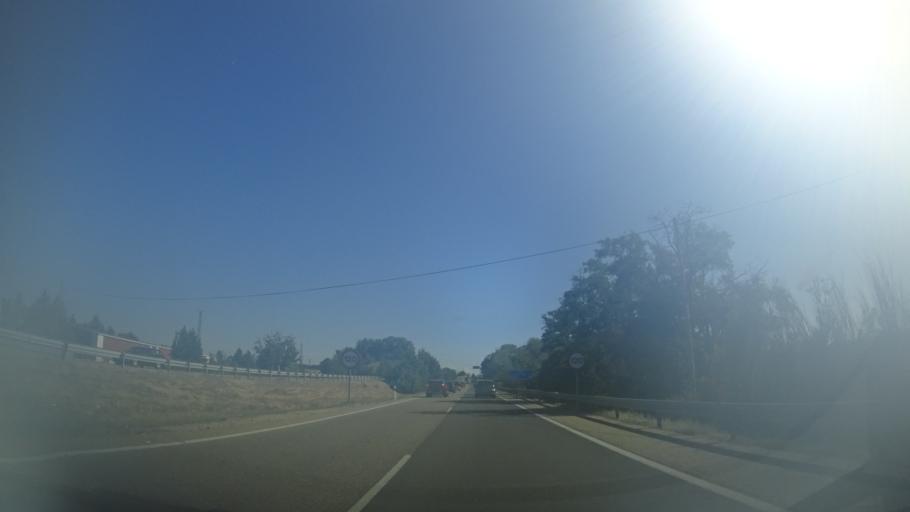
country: ES
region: Castille and Leon
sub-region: Provincia de Valladolid
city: Tordesillas
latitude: 41.4747
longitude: -4.9903
